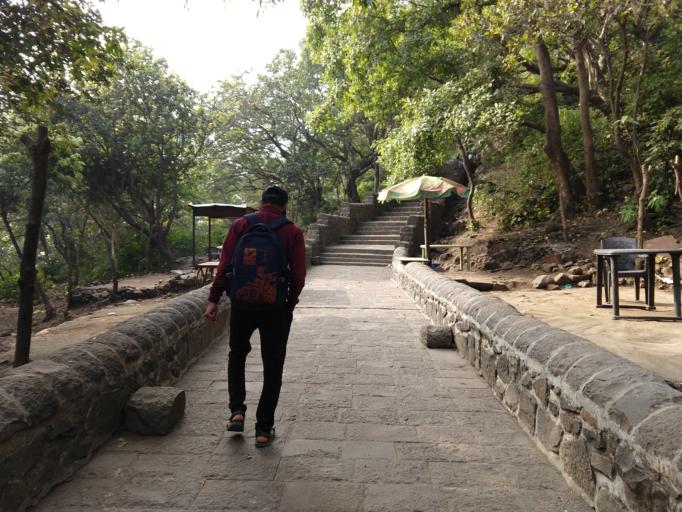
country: IN
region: Maharashtra
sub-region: Pune Division
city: Lonavla
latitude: 18.7083
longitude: 73.4788
